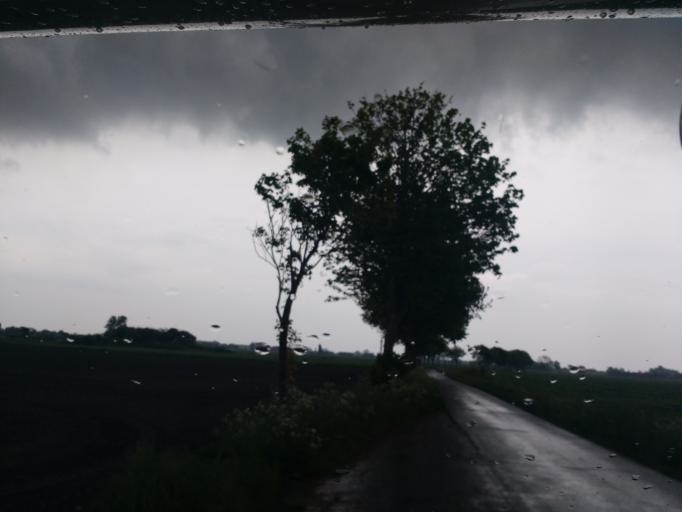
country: DE
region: Lower Saxony
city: Schillig
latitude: 53.7032
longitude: 8.0065
